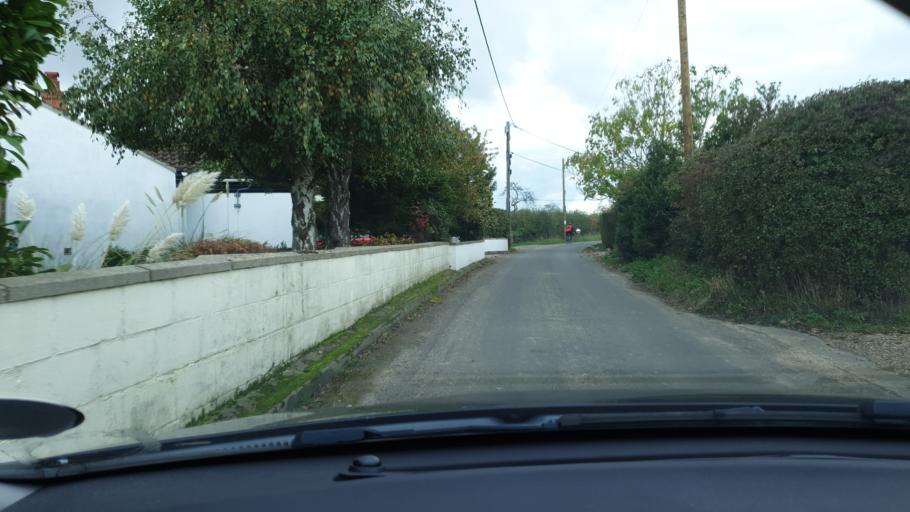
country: GB
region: England
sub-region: Essex
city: Mistley
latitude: 51.9305
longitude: 1.1039
